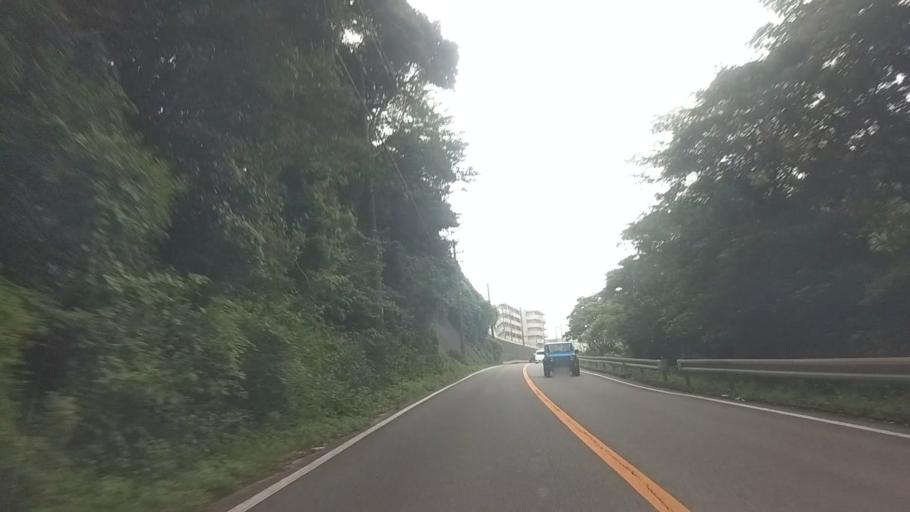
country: JP
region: Chiba
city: Katsuura
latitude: 35.1612
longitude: 140.3191
